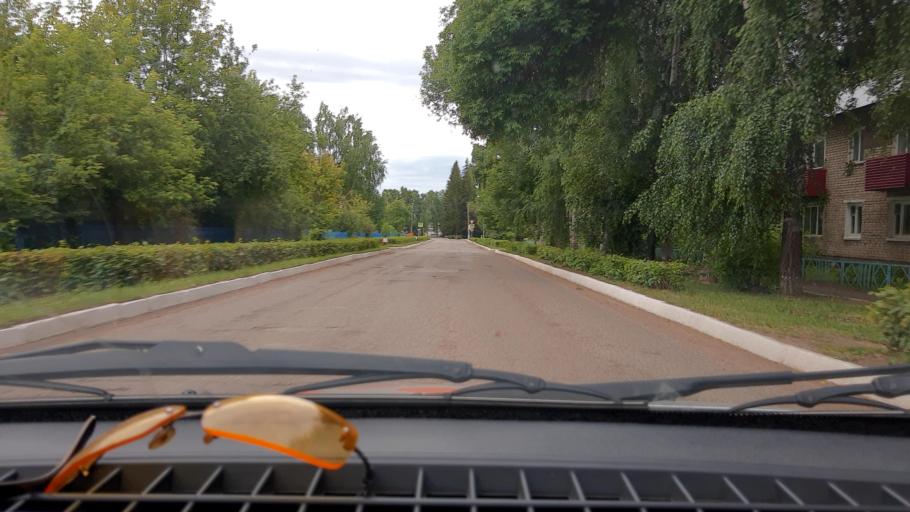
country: RU
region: Bashkortostan
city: Chishmy
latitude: 54.5878
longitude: 55.3804
